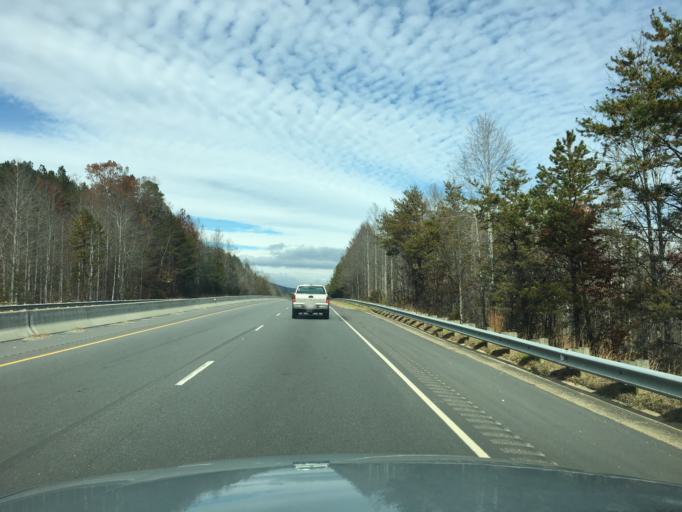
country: US
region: North Carolina
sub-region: McDowell County
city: Marion
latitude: 35.6887
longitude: -82.0305
